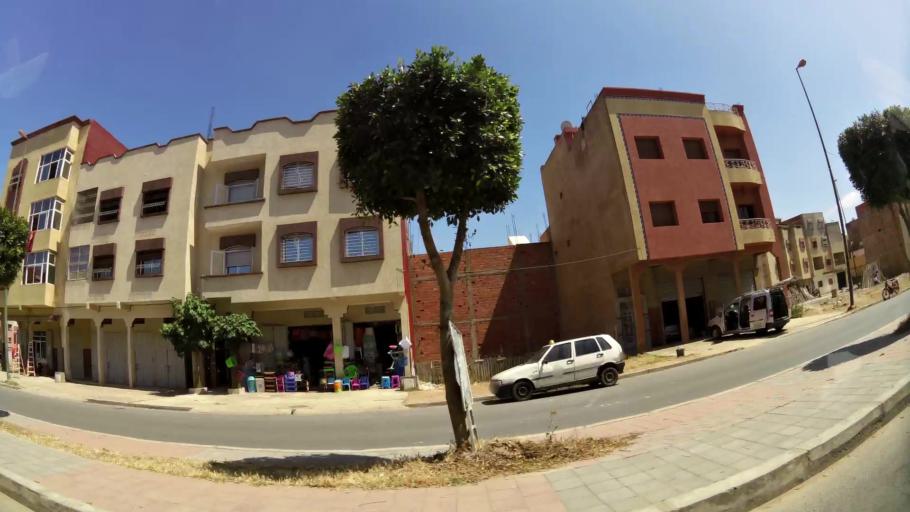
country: MA
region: Gharb-Chrarda-Beni Hssen
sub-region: Kenitra Province
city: Kenitra
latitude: 34.2460
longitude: -6.5387
